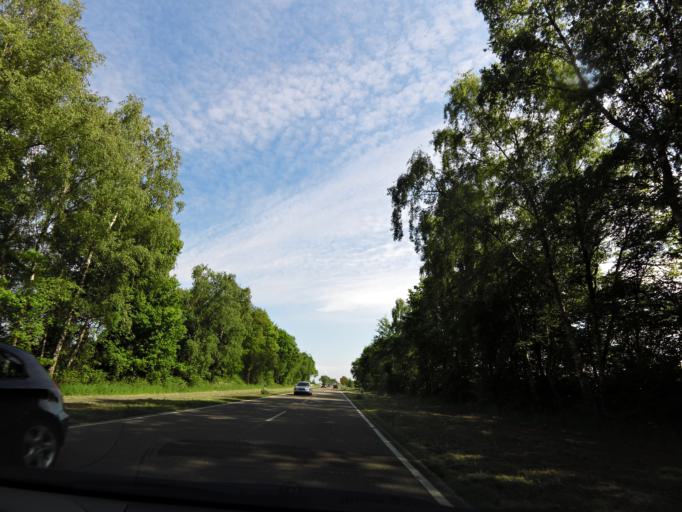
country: DE
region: North Rhine-Westphalia
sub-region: Regierungsbezirk Koln
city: Selfkant
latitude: 50.9984
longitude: 5.9563
